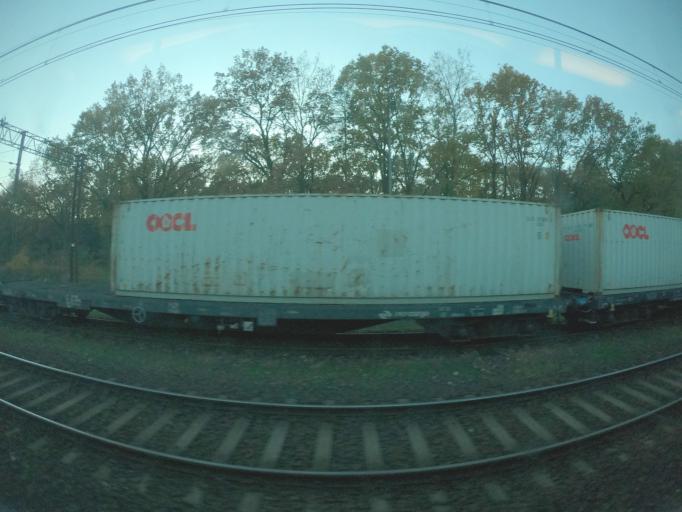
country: PL
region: Lubusz
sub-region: Powiat gorzowski
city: Kostrzyn nad Odra
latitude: 52.6048
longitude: 14.6449
